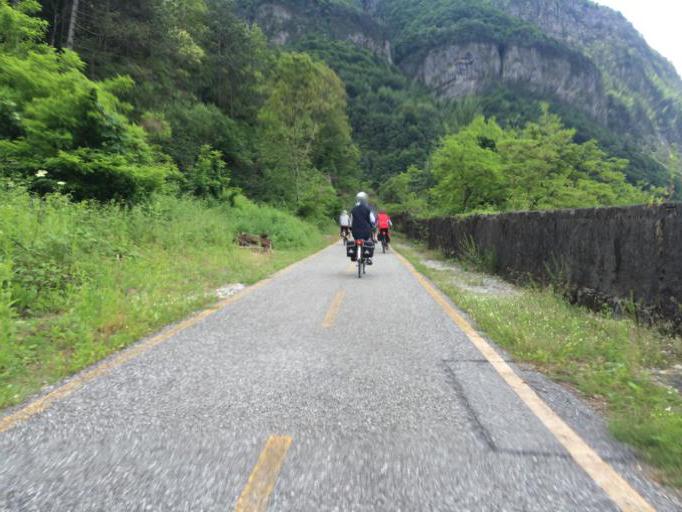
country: IT
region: Friuli Venezia Giulia
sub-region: Provincia di Udine
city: Dogna
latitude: 46.4510
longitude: 13.3177
